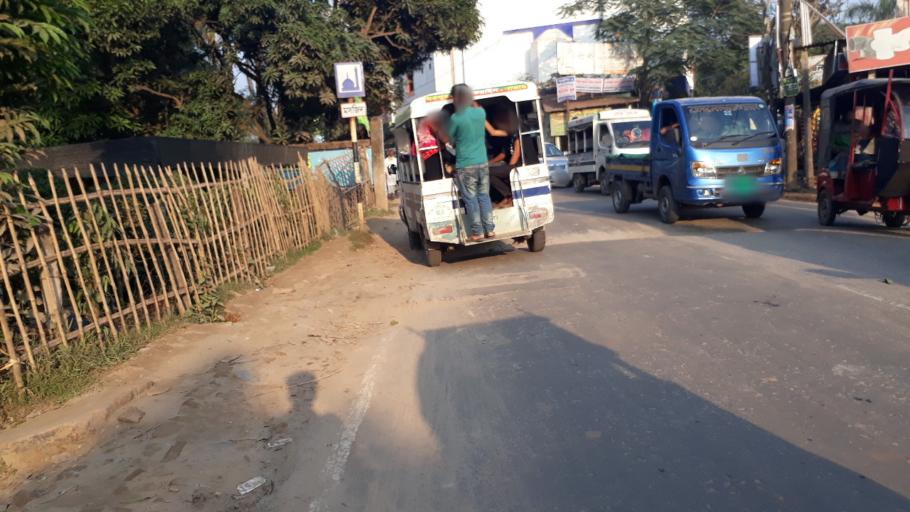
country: BD
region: Dhaka
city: Tungi
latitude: 23.8821
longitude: 90.3014
